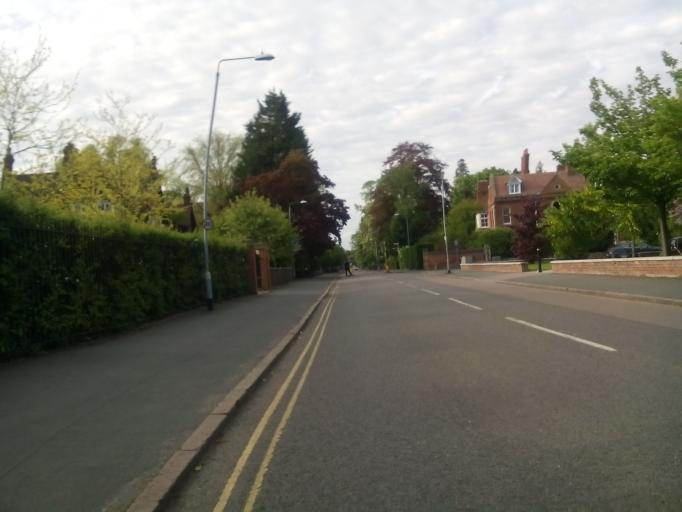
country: GB
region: England
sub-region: Cambridgeshire
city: Cambridge
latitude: 52.2025
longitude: 0.1057
